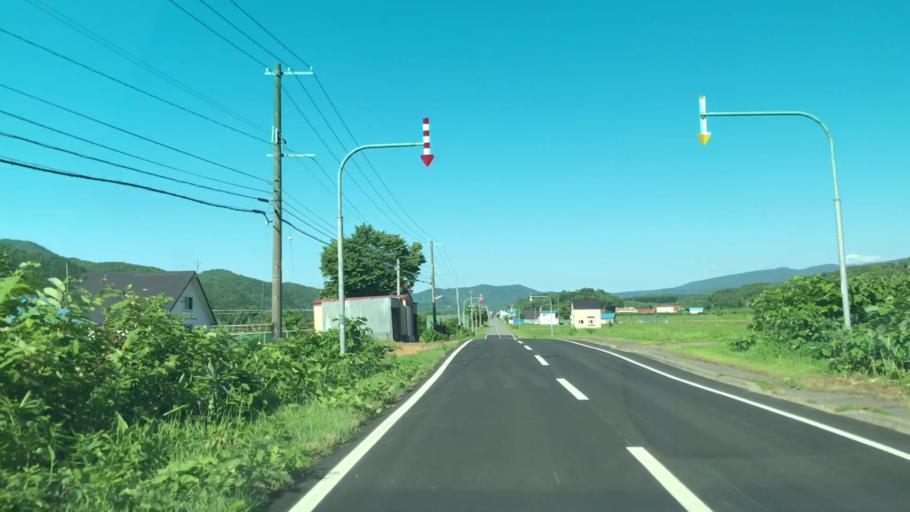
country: JP
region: Hokkaido
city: Yoichi
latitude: 43.0344
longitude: 140.7781
